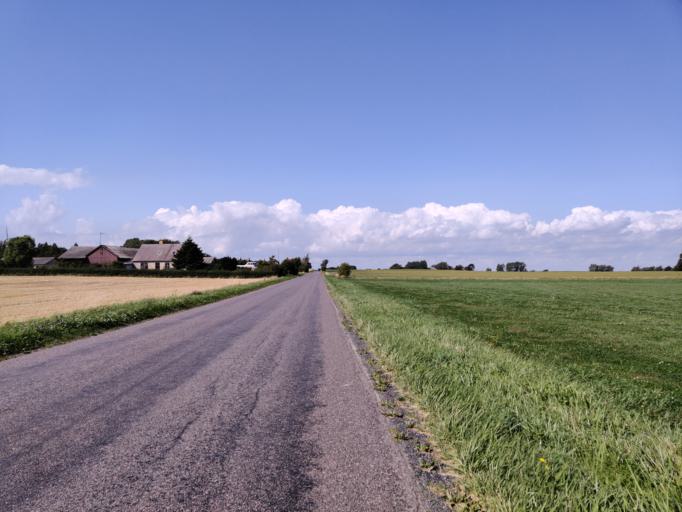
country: DK
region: Zealand
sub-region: Guldborgsund Kommune
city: Nykobing Falster
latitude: 54.6062
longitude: 11.9270
